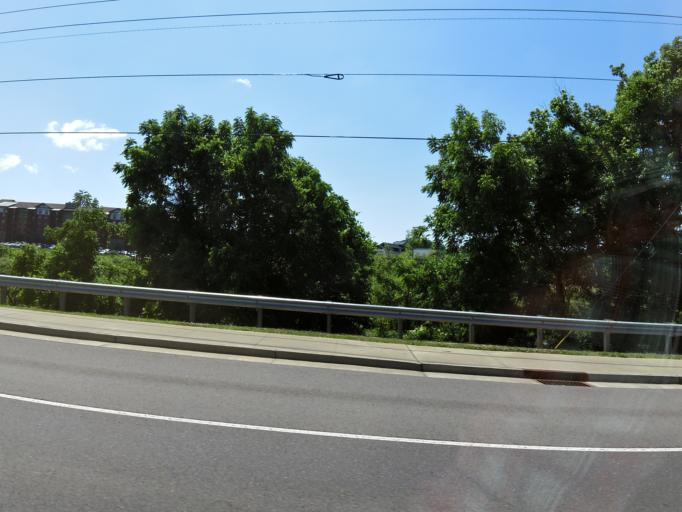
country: US
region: Tennessee
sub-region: Sevier County
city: Sevierville
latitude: 35.8959
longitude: -83.5812
